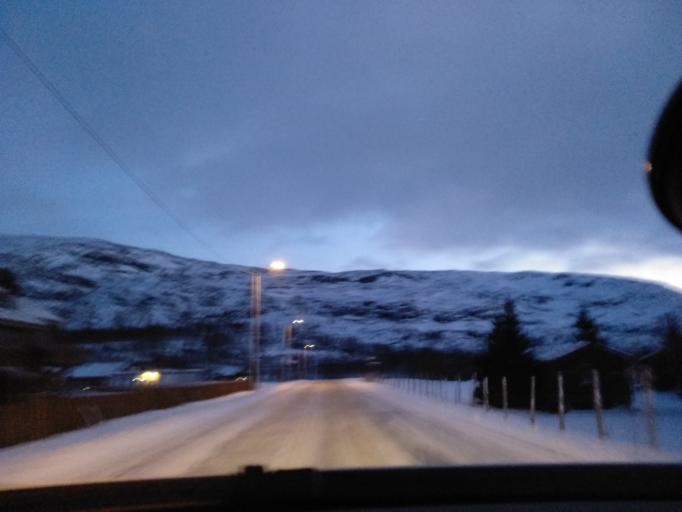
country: NO
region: Vest-Agder
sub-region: Sirdal
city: Tonstad
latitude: 59.0148
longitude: 6.9382
